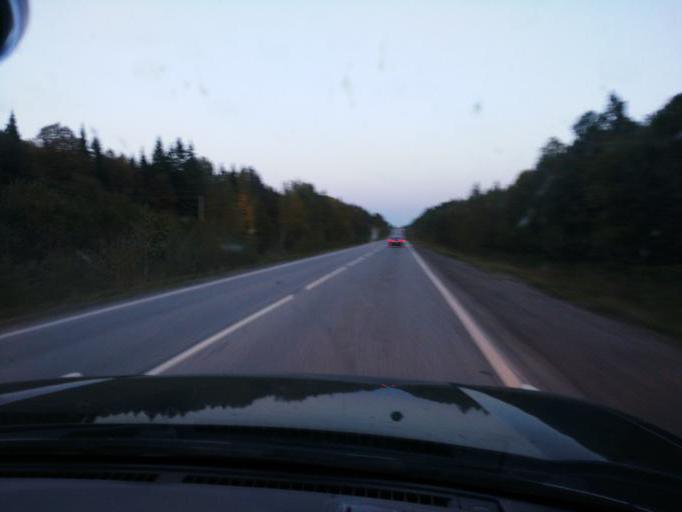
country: RU
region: Perm
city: Verkhnechusovskiye Gorodki
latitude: 58.2735
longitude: 56.9424
